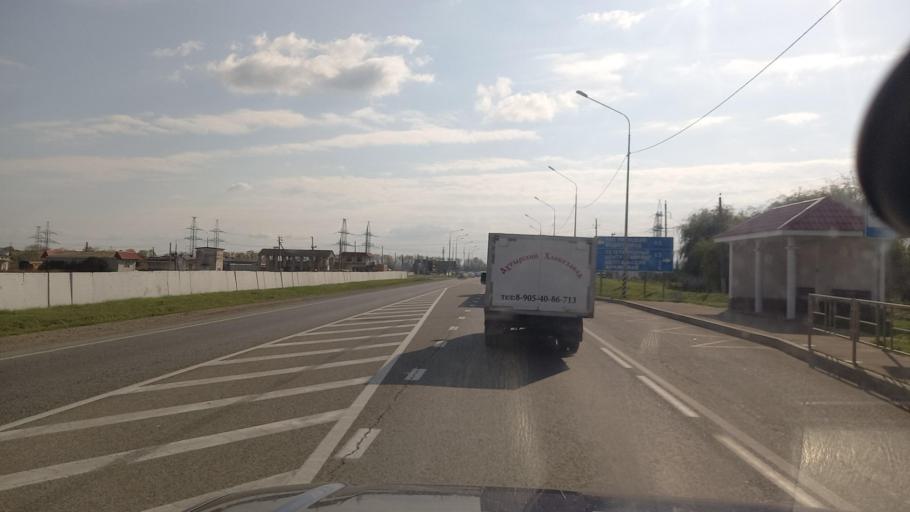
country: RU
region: Krasnodarskiy
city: Novoukrainskiy
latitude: 44.9067
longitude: 38.0265
